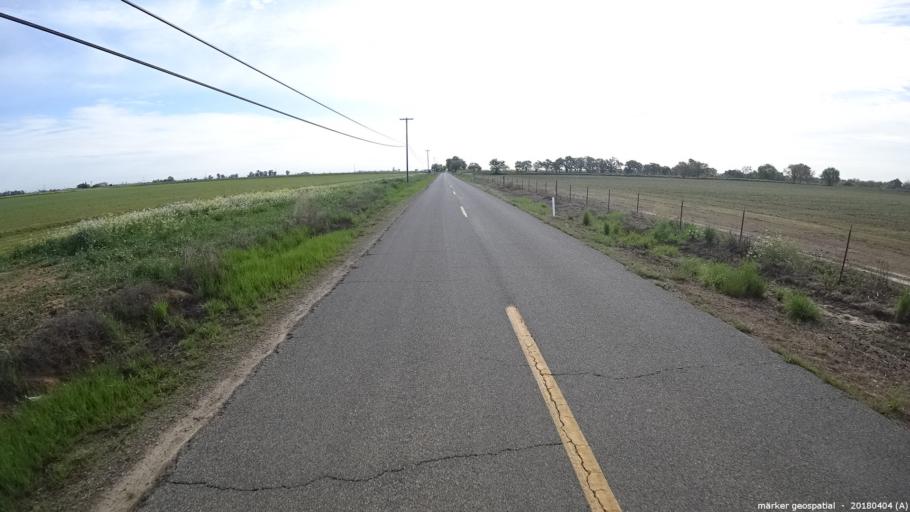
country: US
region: California
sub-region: Sacramento County
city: Herald
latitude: 38.2557
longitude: -121.2309
